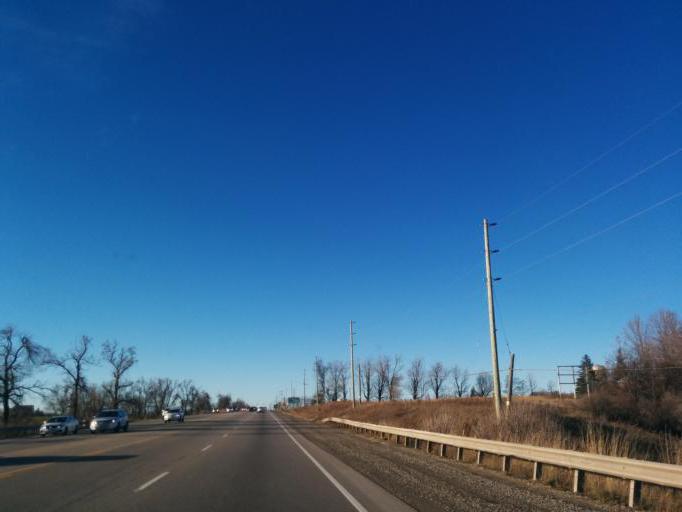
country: CA
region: Ontario
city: Brampton
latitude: 43.7502
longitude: -79.8467
